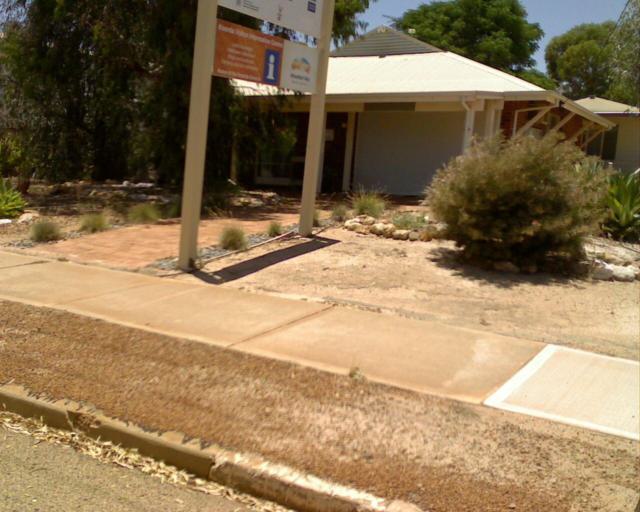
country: AU
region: Western Australia
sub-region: Wongan-Ballidu
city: Wongan Hills
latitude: -30.8265
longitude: 117.4812
